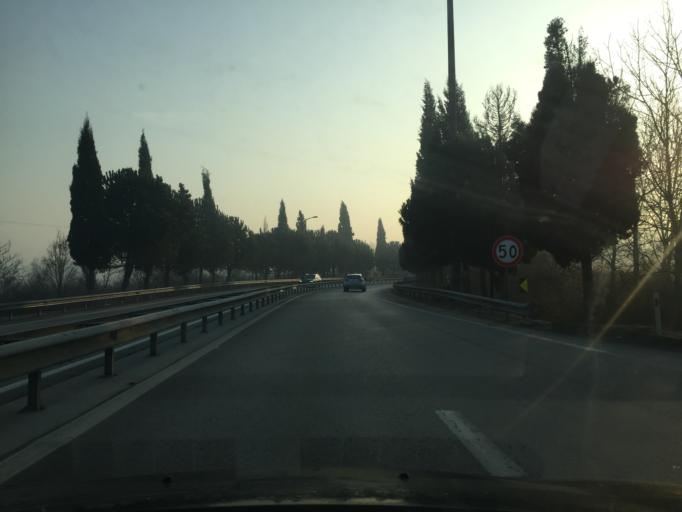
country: TR
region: Sakarya
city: Akyazi
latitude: 40.7217
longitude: 30.5659
